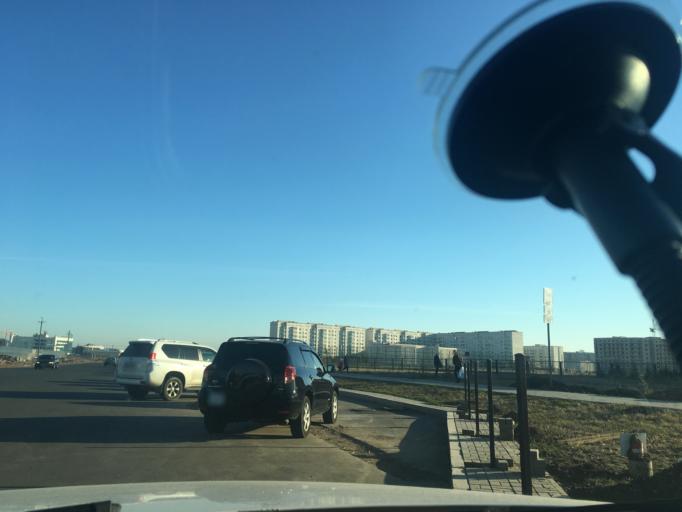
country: KZ
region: Astana Qalasy
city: Astana
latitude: 51.1404
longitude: 71.3706
